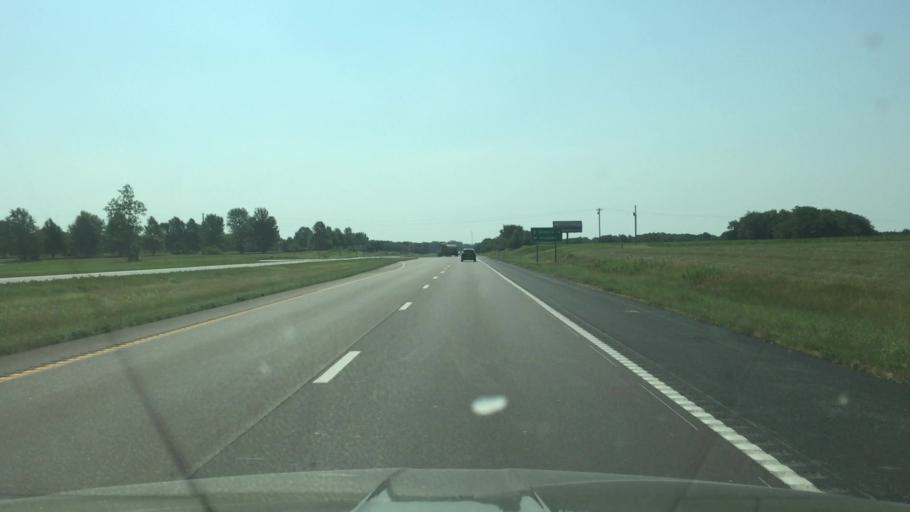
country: US
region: Missouri
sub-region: Pettis County
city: La Monte
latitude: 38.7485
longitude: -93.3435
